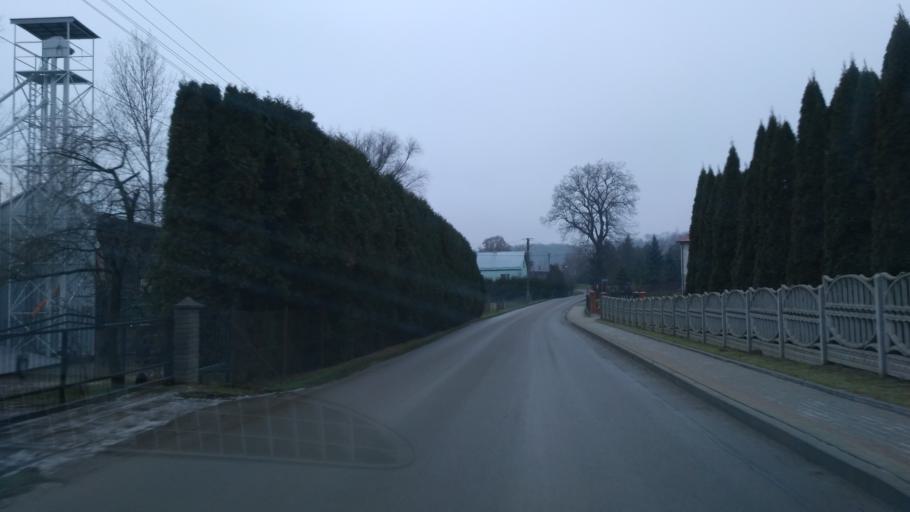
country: PL
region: Subcarpathian Voivodeship
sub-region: Powiat przeworski
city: Zarzecze
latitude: 49.9900
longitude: 22.5266
